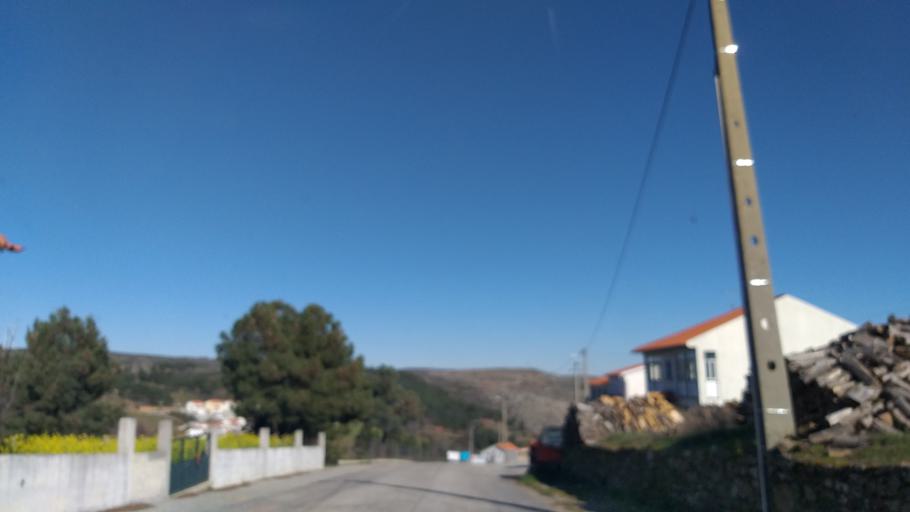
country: PT
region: Guarda
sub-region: Celorico da Beira
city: Celorico da Beira
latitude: 40.5169
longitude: -7.3997
